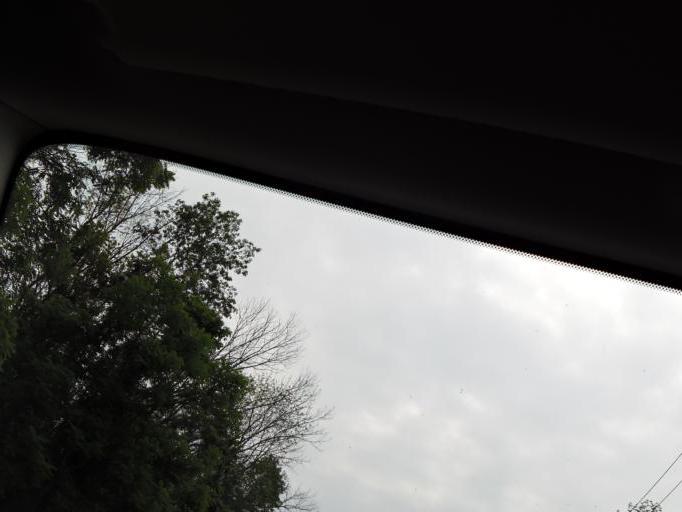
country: US
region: Ohio
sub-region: Clinton County
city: Blanchester
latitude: 39.2893
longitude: -83.9117
